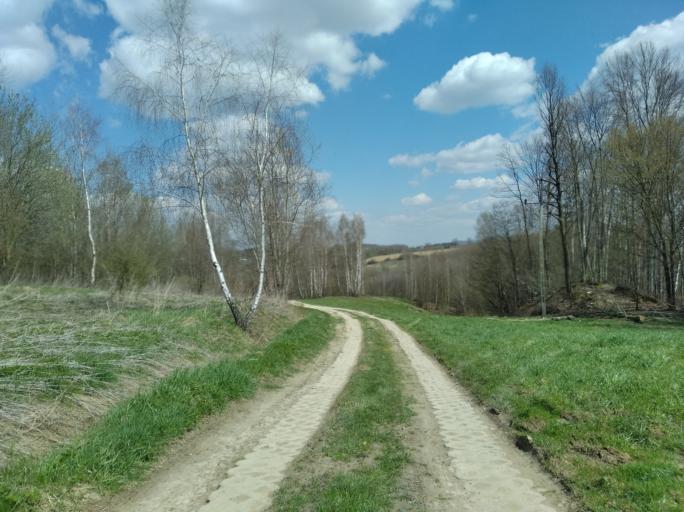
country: PL
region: Subcarpathian Voivodeship
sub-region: Powiat strzyzowski
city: Wysoka Strzyzowska
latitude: 49.8442
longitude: 21.7578
